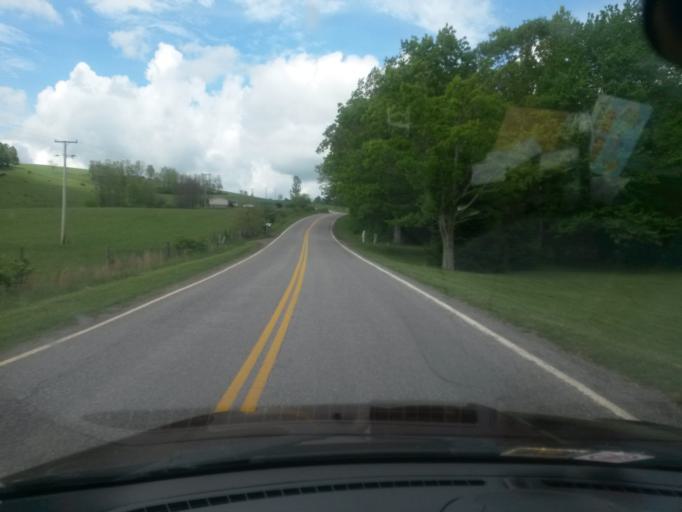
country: US
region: Virginia
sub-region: Floyd County
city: Floyd
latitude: 36.7598
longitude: -80.3903
